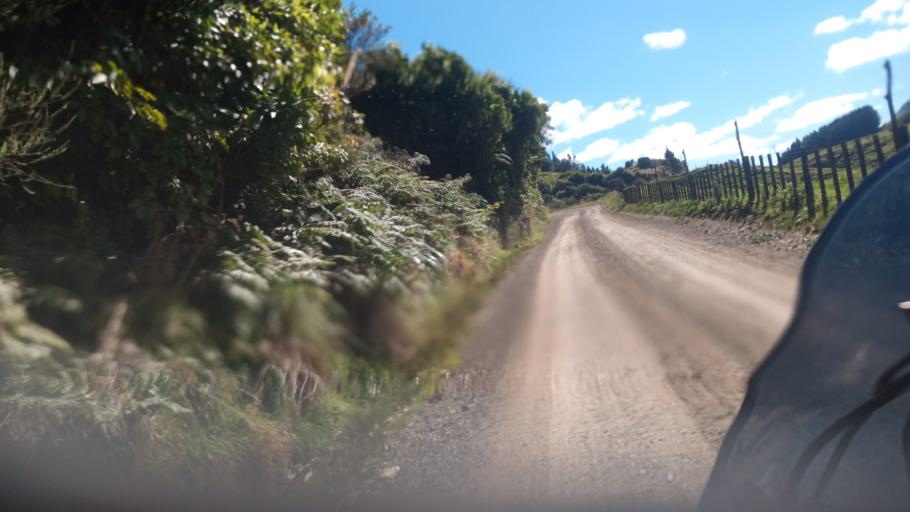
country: NZ
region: Bay of Plenty
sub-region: Opotiki District
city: Opotiki
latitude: -38.3381
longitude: 177.5795
